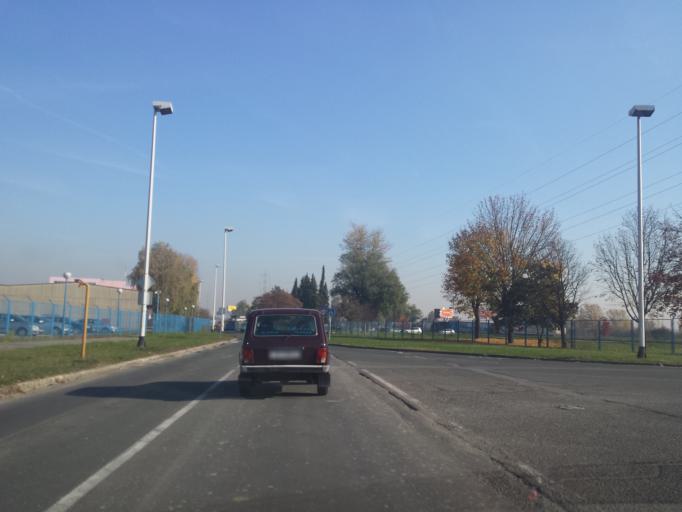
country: HR
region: Grad Zagreb
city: Stenjevec
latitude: 45.7990
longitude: 15.8728
